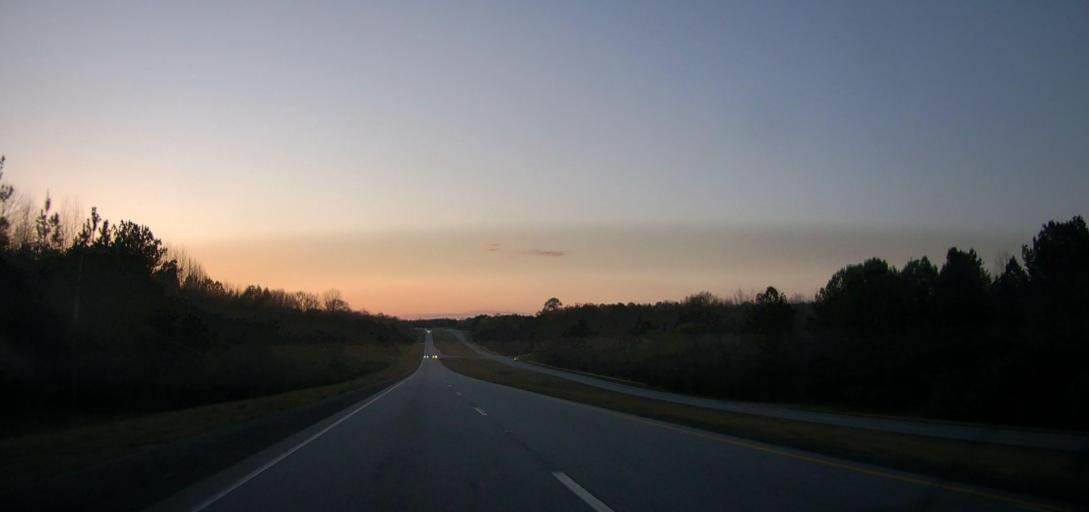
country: US
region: Alabama
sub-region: Tallapoosa County
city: Dadeville
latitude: 32.8719
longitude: -85.8074
